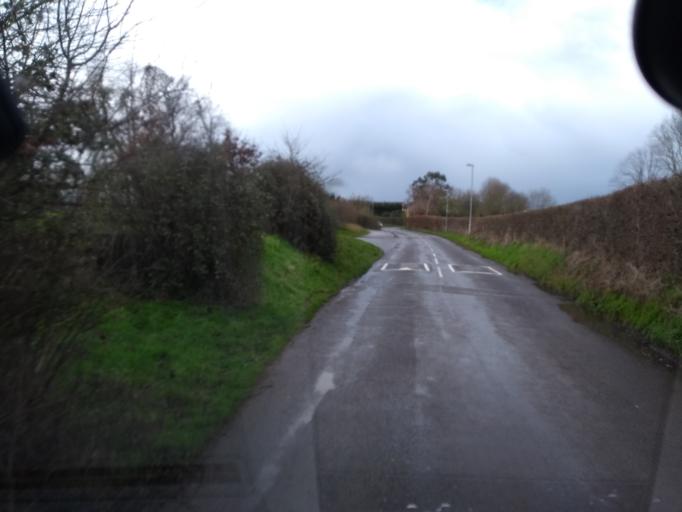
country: GB
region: England
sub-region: Somerset
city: Creech Saint Michael
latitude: 51.0191
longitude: -3.0556
